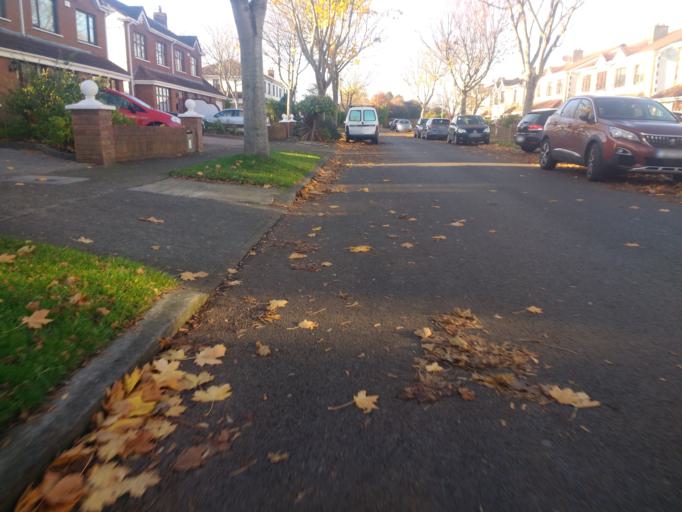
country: IE
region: Leinster
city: Kinsealy-Drinan
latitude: 53.4527
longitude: -6.1871
